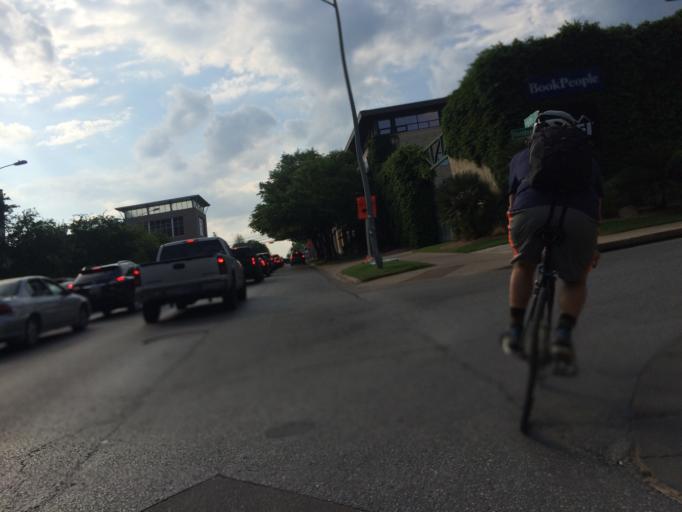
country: US
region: Texas
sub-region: Travis County
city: Austin
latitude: 30.2712
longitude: -97.7528
